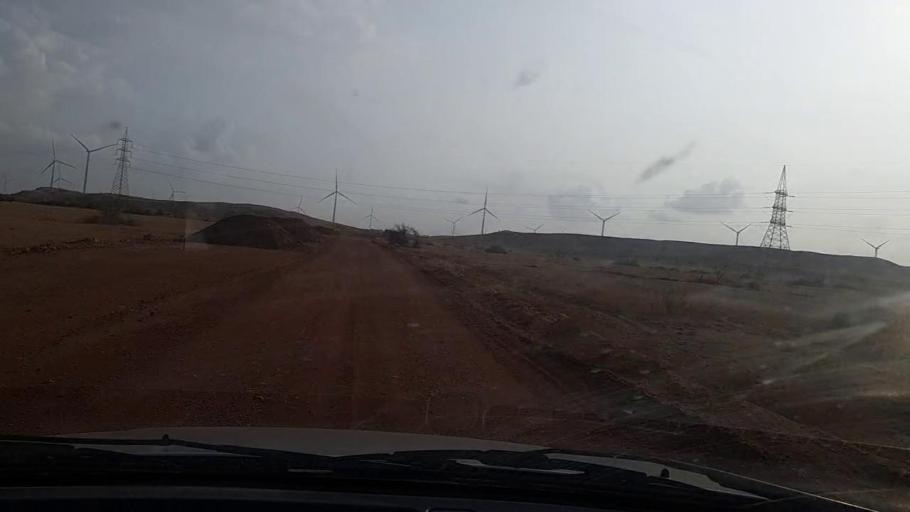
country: PK
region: Sindh
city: Thatta
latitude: 25.0532
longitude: 67.8743
